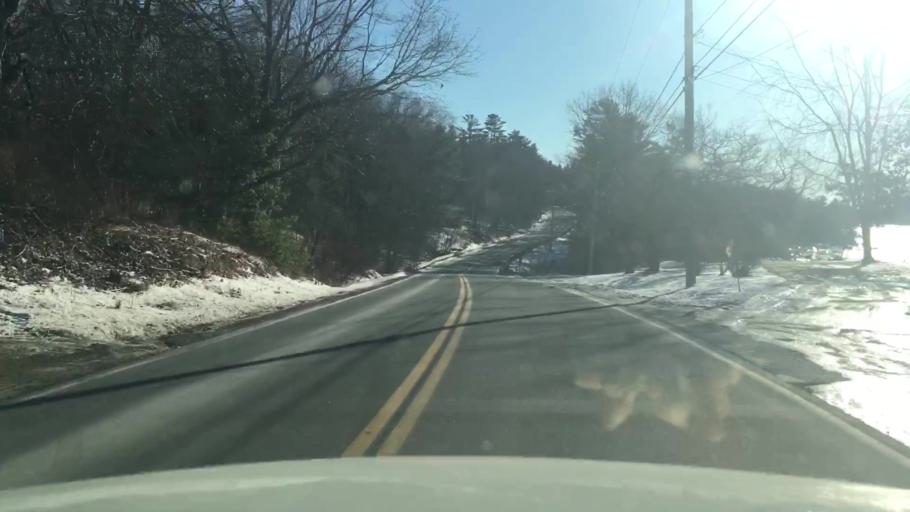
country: US
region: Maine
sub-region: Hancock County
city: Orland
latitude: 44.5419
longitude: -68.7453
